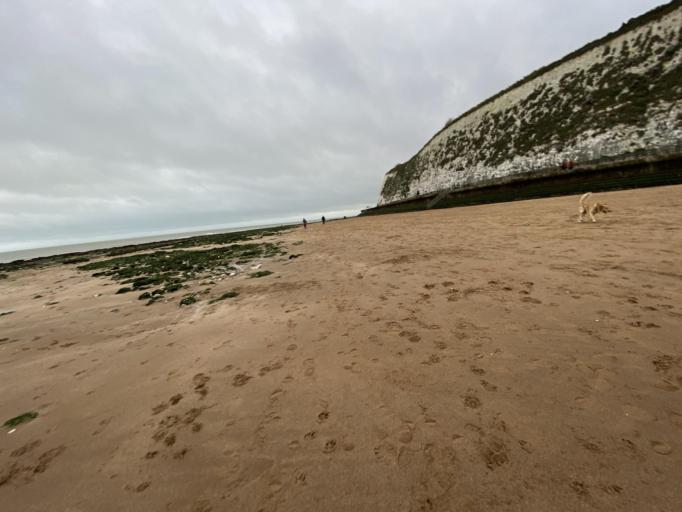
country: GB
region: England
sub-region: Kent
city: Broadstairs
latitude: 51.3513
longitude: 1.4429
